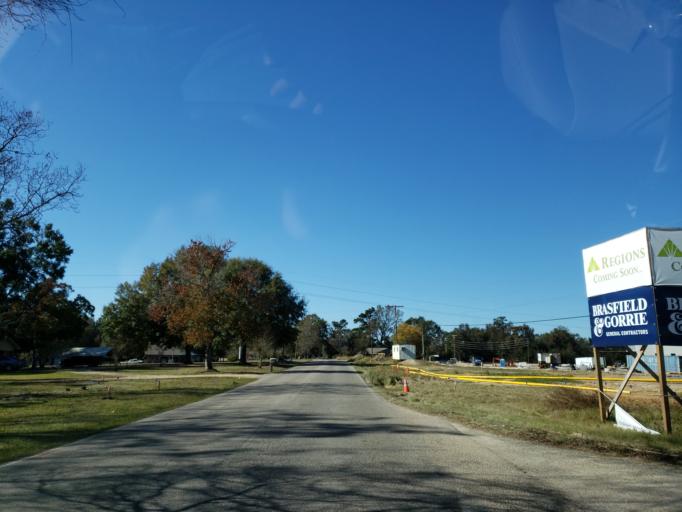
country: US
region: Mississippi
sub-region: Lamar County
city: West Hattiesburg
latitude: 31.3095
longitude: -89.3954
